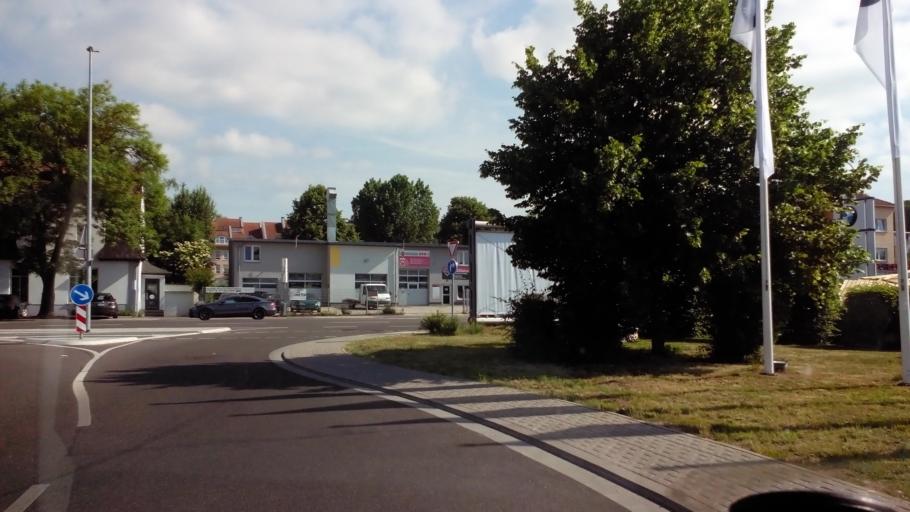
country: DE
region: Saarland
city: Saarlouis
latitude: 49.3248
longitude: 6.7500
